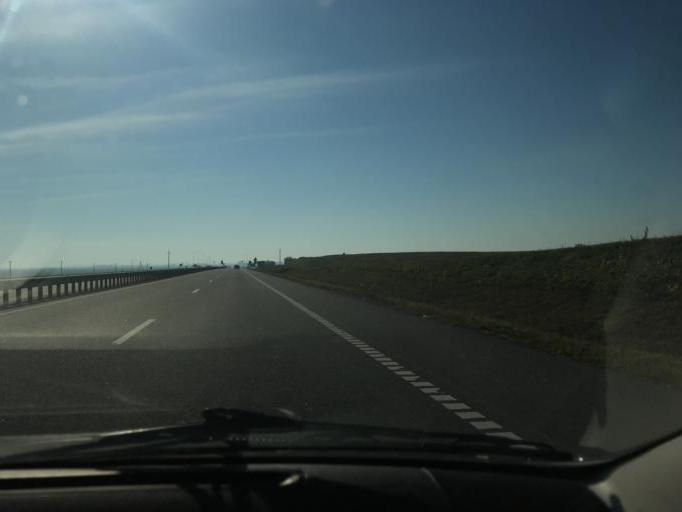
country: BY
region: Minsk
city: Slutsk
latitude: 53.1812
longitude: 27.5511
